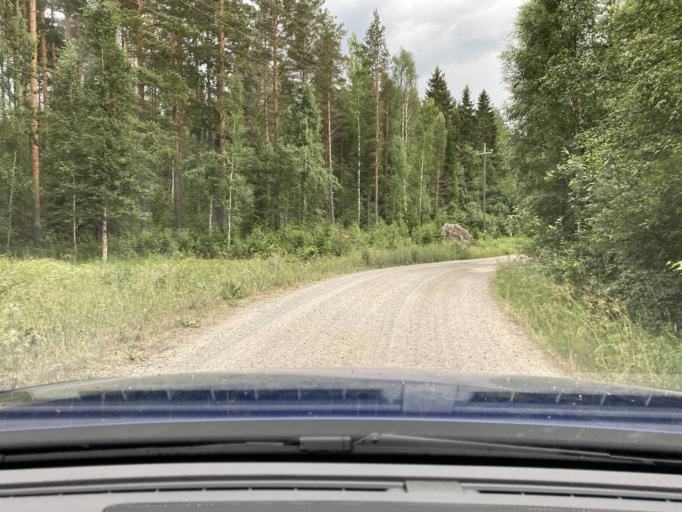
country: FI
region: Satakunta
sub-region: Rauma
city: Lappi
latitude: 61.1413
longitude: 21.9074
